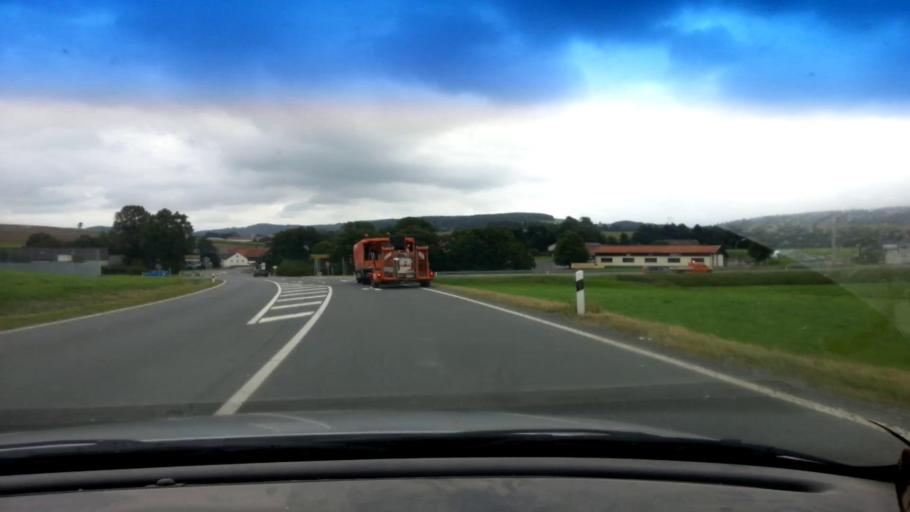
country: DE
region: Bavaria
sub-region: Upper Franconia
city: Gefrees
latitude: 50.0940
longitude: 11.7116
